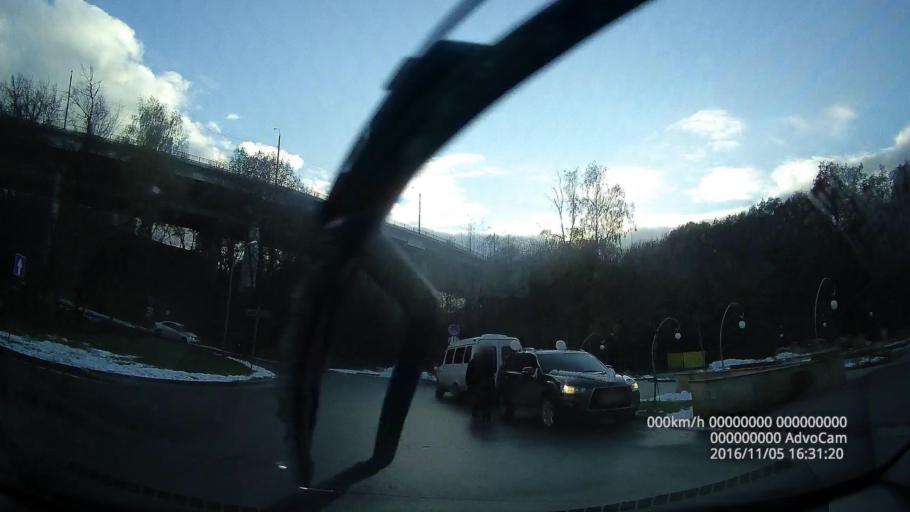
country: RU
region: Voronezj
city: Voronezh
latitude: 51.6915
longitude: 39.2245
